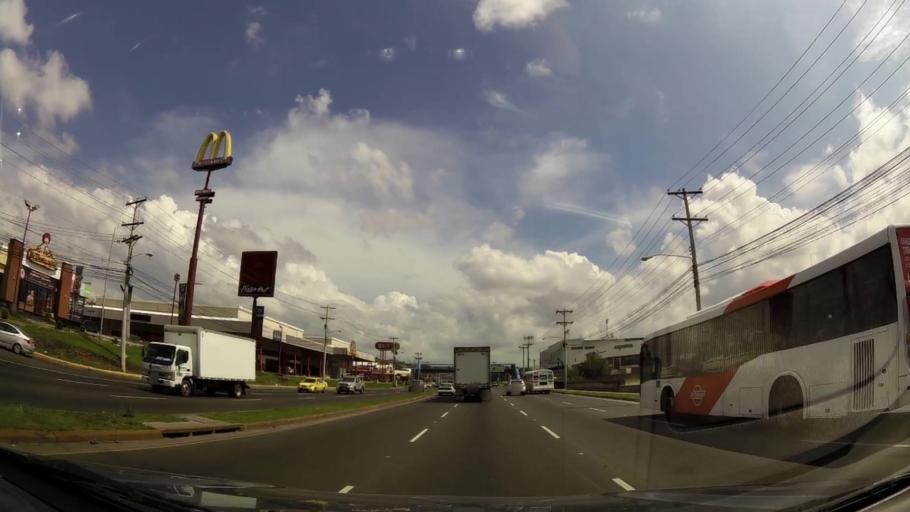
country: PA
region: Panama
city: San Miguelito
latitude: 9.0369
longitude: -79.4817
